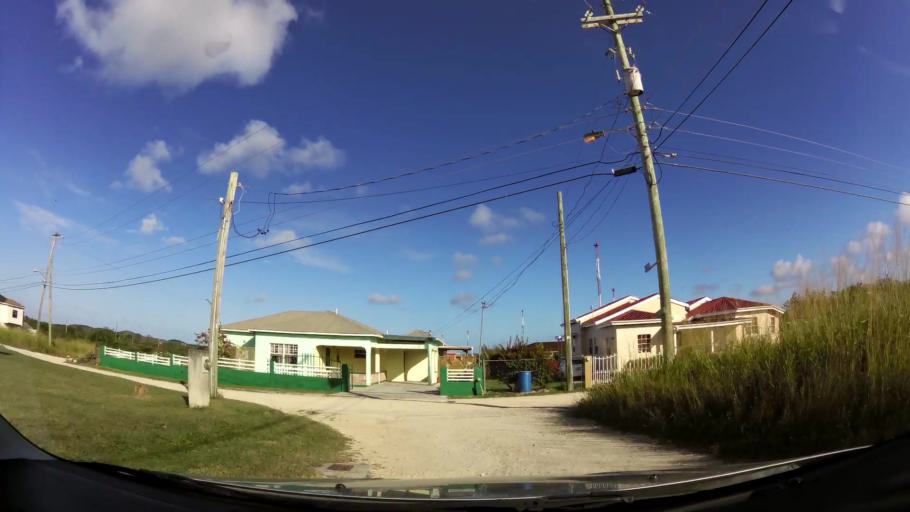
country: AG
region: Saint George
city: Piggotts
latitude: 17.1009
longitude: -61.8025
